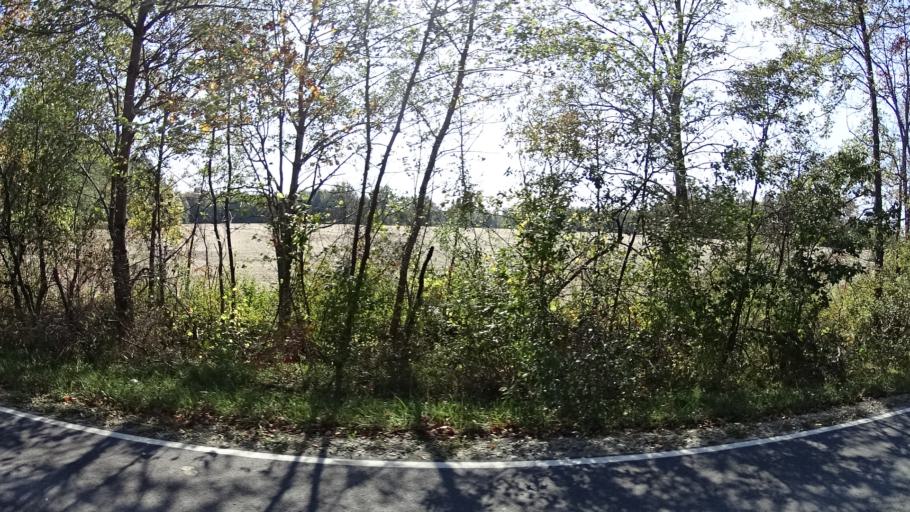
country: US
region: Ohio
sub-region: Lorain County
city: Vermilion-on-the-Lake
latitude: 41.4015
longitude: -82.3103
